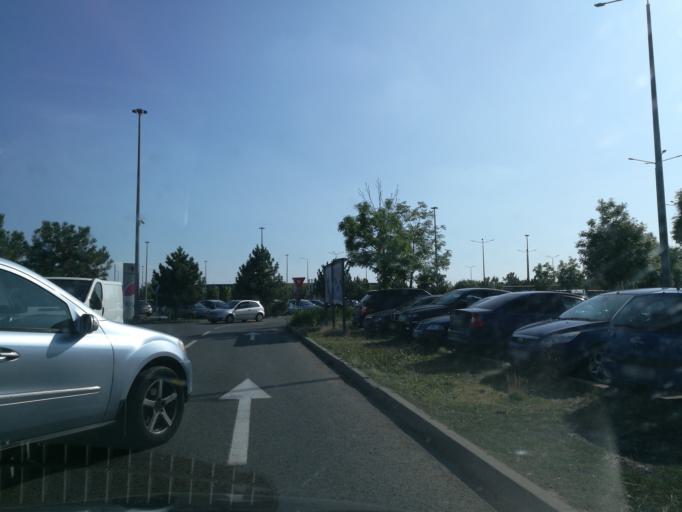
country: RO
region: Ilfov
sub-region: Comuna Otopeni
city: Otopeni
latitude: 44.5098
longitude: 26.0865
